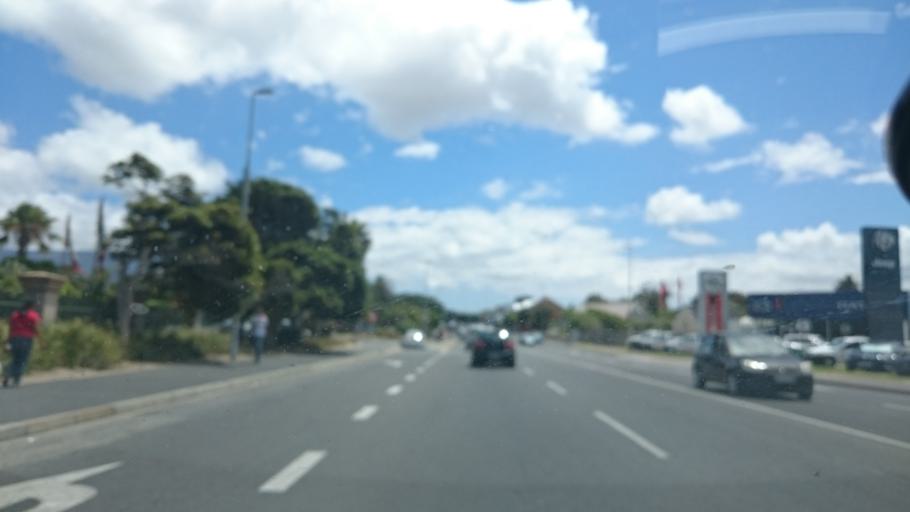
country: ZA
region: Western Cape
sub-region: City of Cape Town
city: Bergvliet
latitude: -34.0647
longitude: 18.4590
